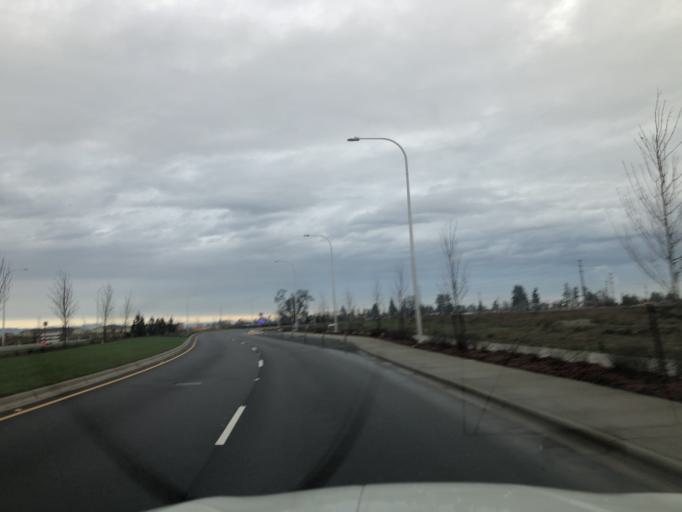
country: US
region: Oregon
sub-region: Washington County
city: Aloha
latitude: 45.4943
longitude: -122.9005
